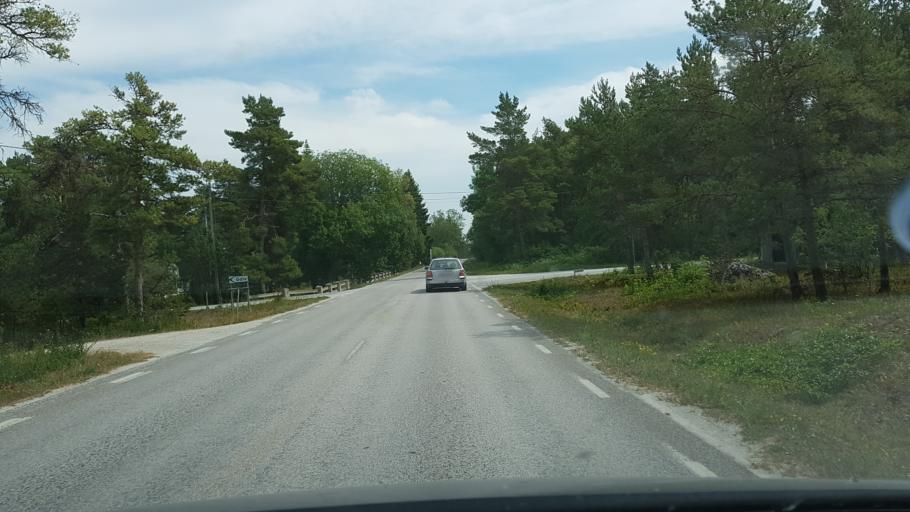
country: SE
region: Gotland
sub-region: Gotland
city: Slite
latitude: 57.7277
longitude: 18.7525
